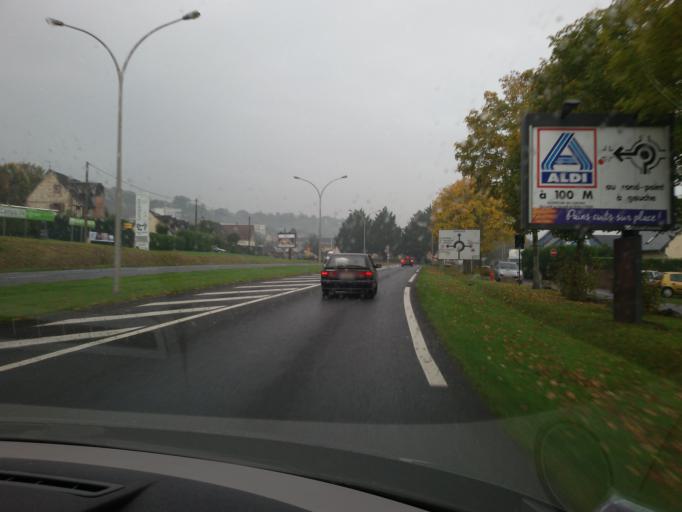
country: FR
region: Lower Normandy
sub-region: Departement du Calvados
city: La Riviere-Saint-Sauveur
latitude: 49.4111
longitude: 0.2548
